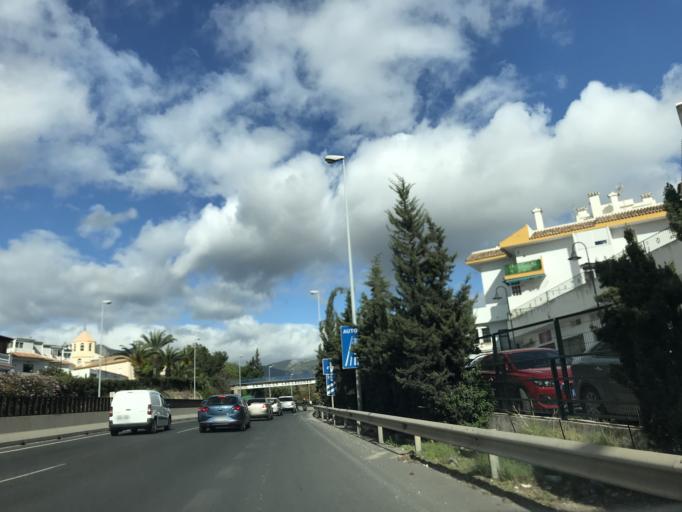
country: ES
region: Andalusia
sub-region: Provincia de Malaga
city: Fuengirola
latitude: 36.5419
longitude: -4.6348
